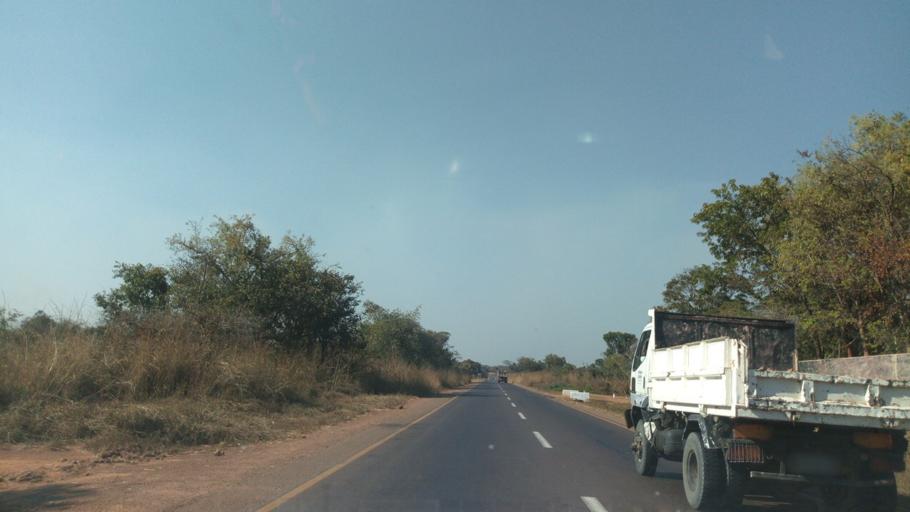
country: CD
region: Katanga
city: Lubumbashi
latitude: -11.4688
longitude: 27.6606
